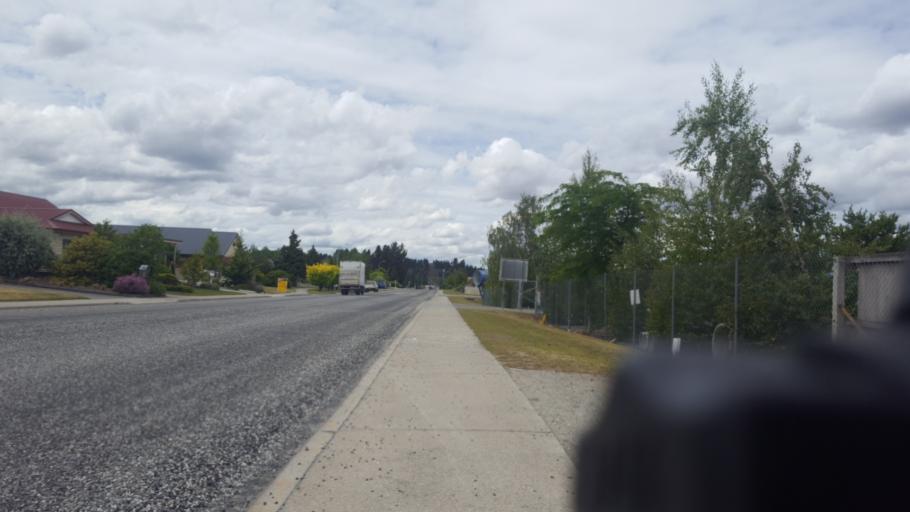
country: NZ
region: Otago
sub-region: Queenstown-Lakes District
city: Wanaka
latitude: -45.2466
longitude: 169.3754
